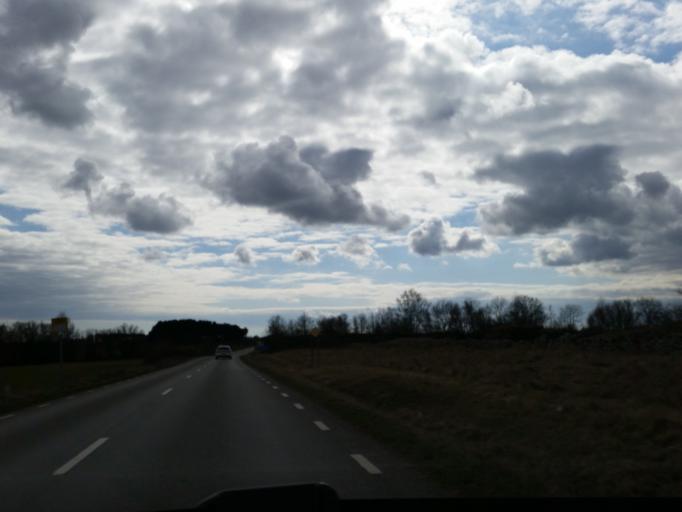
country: SE
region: Kalmar
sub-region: Morbylanga Kommun
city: Sodra Sandby
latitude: 56.6699
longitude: 16.6833
